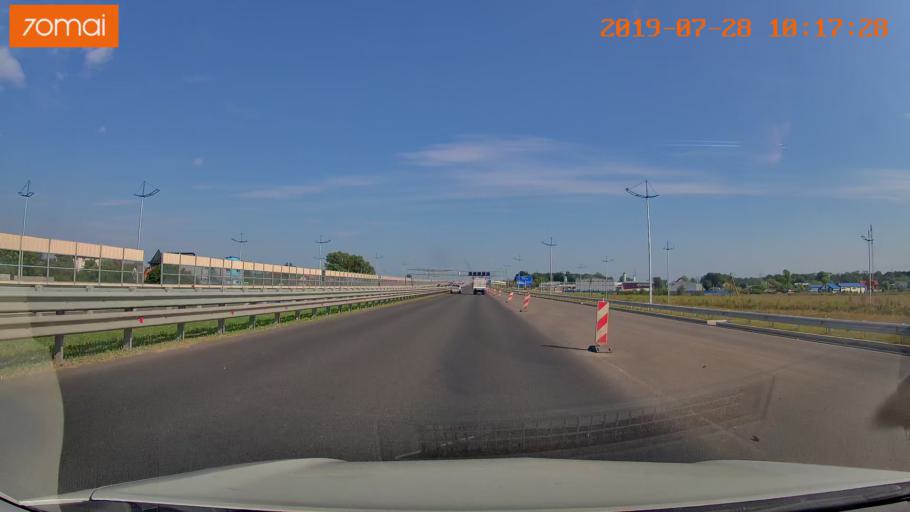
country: RU
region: Kaliningrad
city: Maloye Isakovo
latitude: 54.7403
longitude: 20.5941
